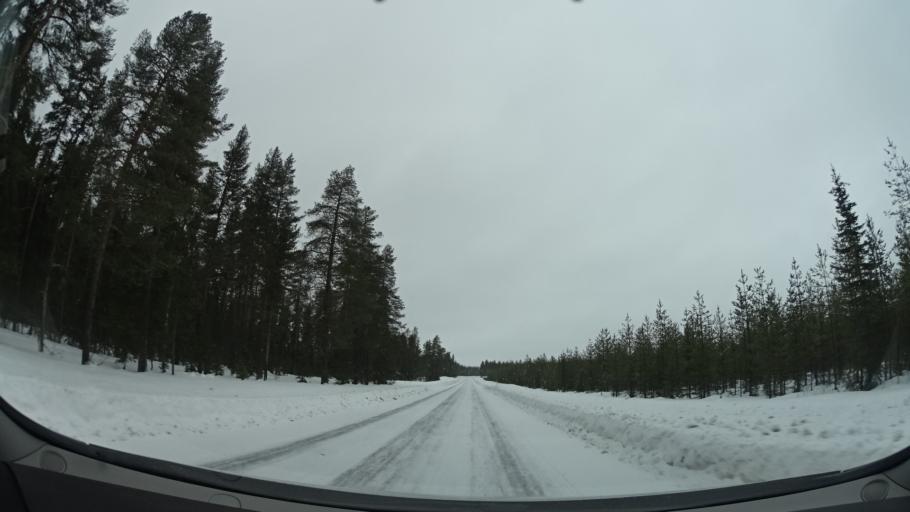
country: SE
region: Vaesterbotten
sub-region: Mala Kommun
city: Mala
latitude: 65.1193
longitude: 18.8795
